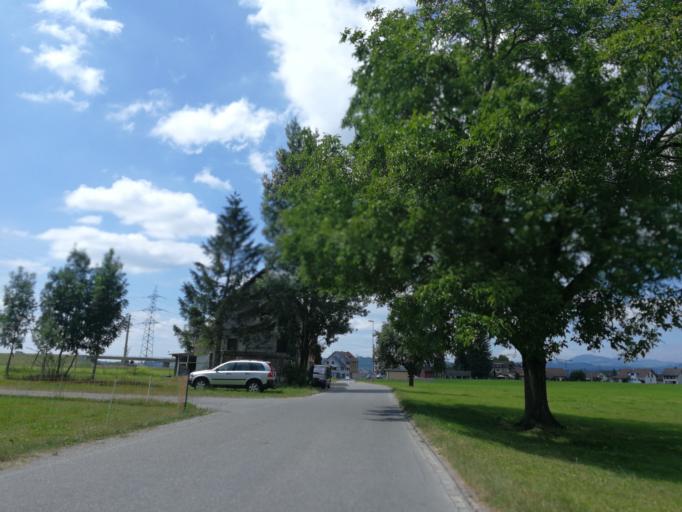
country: CH
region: Saint Gallen
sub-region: Wahlkreis See-Gaster
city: Benken
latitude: 47.1819
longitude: 8.9976
